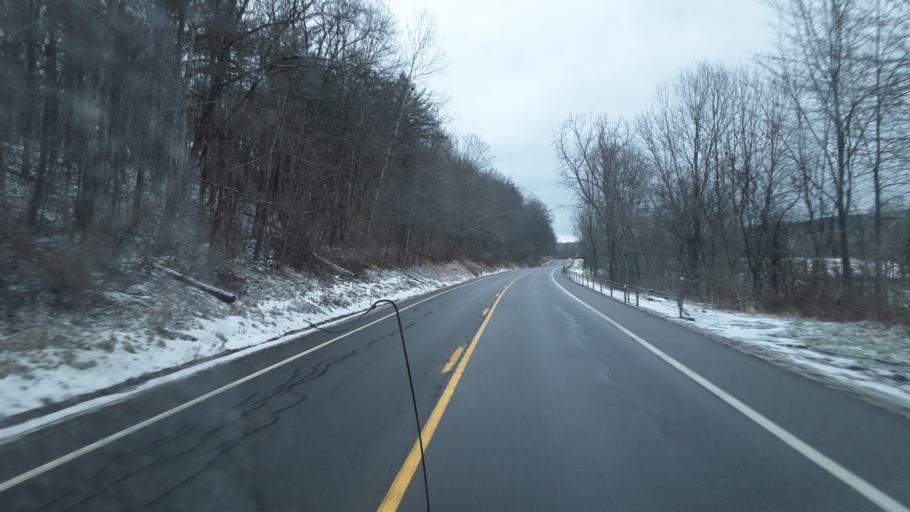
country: US
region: New York
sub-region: Allegany County
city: Belmont
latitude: 42.3186
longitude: -78.0988
